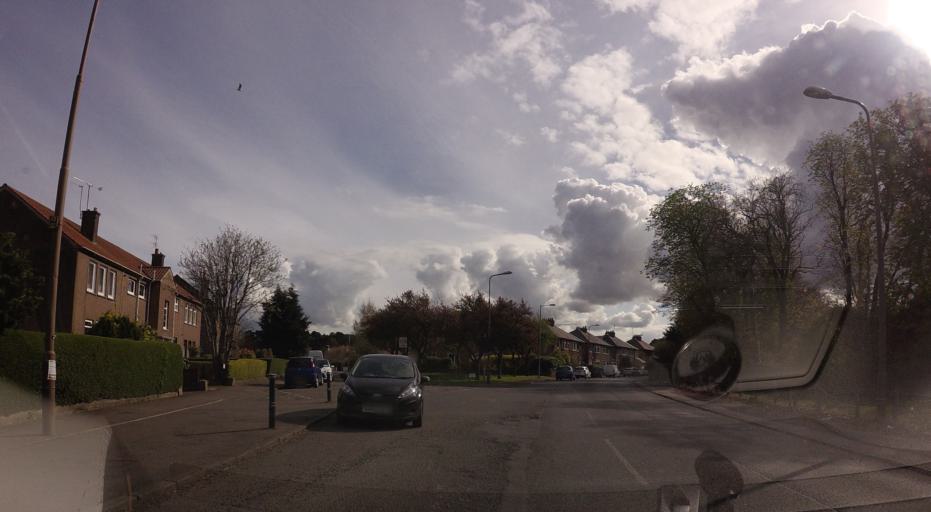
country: GB
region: Scotland
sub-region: Edinburgh
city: Colinton
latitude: 55.9698
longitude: -3.2745
